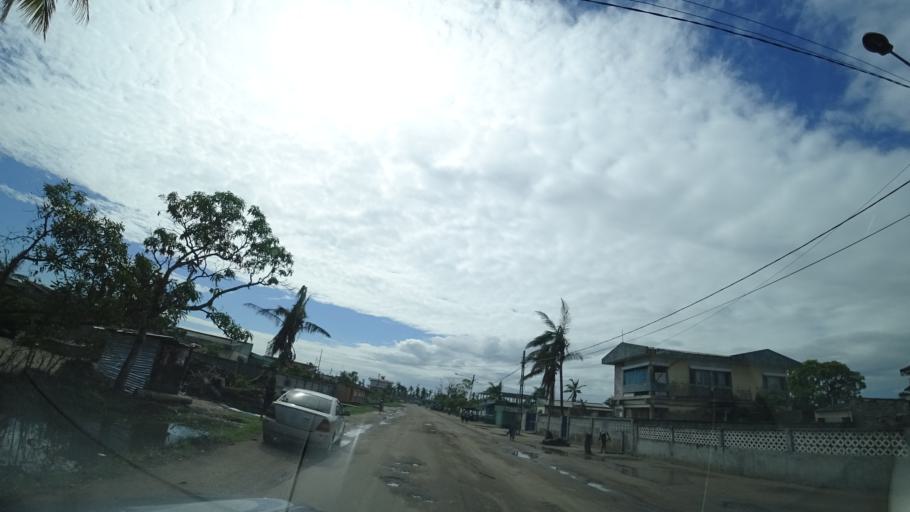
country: MZ
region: Sofala
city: Beira
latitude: -19.7578
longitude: 34.8641
